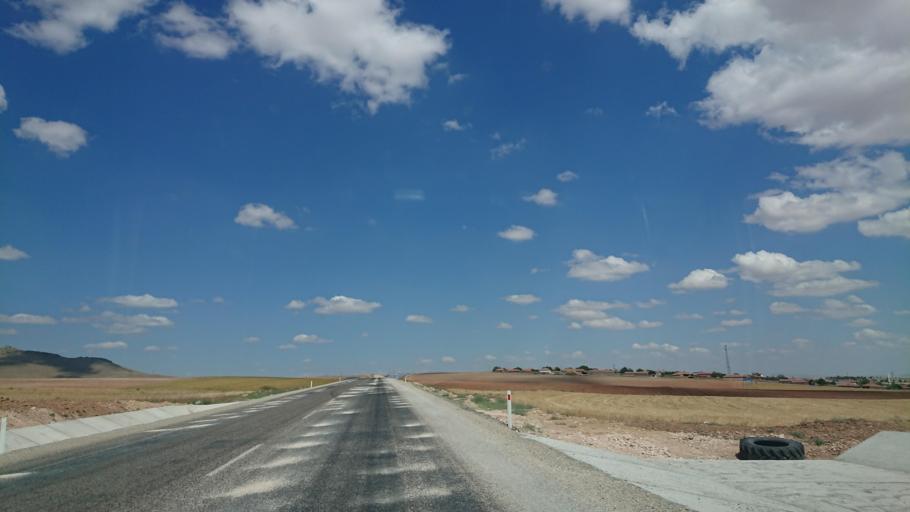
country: TR
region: Kirsehir
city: Kirsehir
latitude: 39.1238
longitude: 33.9780
